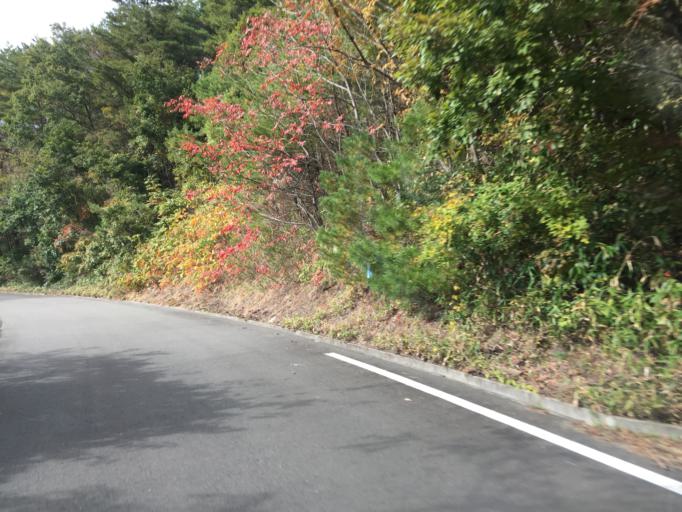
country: JP
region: Miyagi
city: Marumori
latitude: 37.8031
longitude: 140.7576
